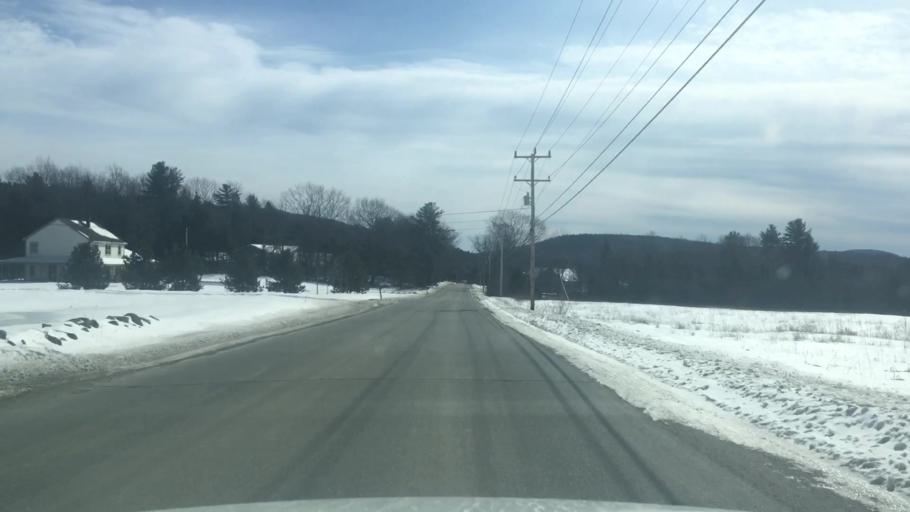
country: US
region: Maine
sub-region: Penobscot County
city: Holden
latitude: 44.7445
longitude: -68.6307
